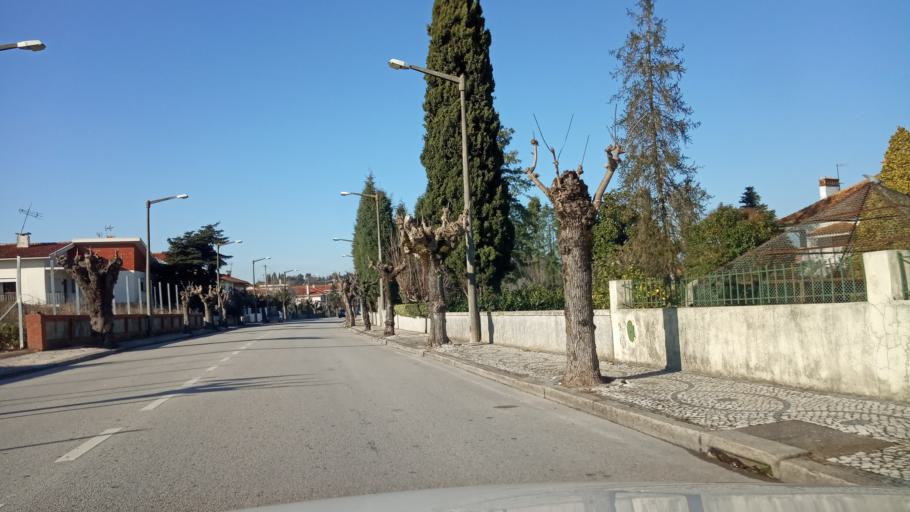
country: PT
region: Aveiro
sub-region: Anadia
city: Anadia
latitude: 40.4356
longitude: -8.4336
